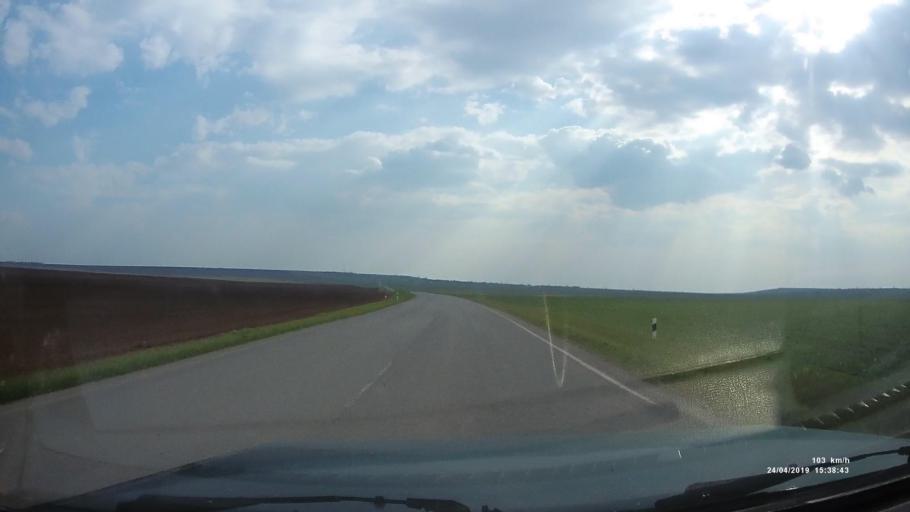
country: RU
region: Kalmykiya
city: Yashalta
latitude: 46.5946
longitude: 42.8236
